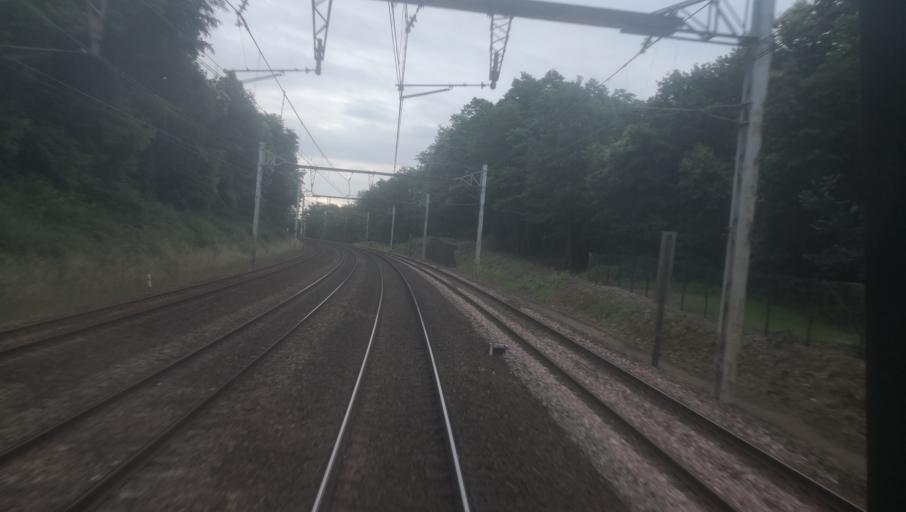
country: FR
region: Ile-de-France
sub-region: Departement de l'Essonne
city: Chamarande
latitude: 48.5155
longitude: 2.2342
